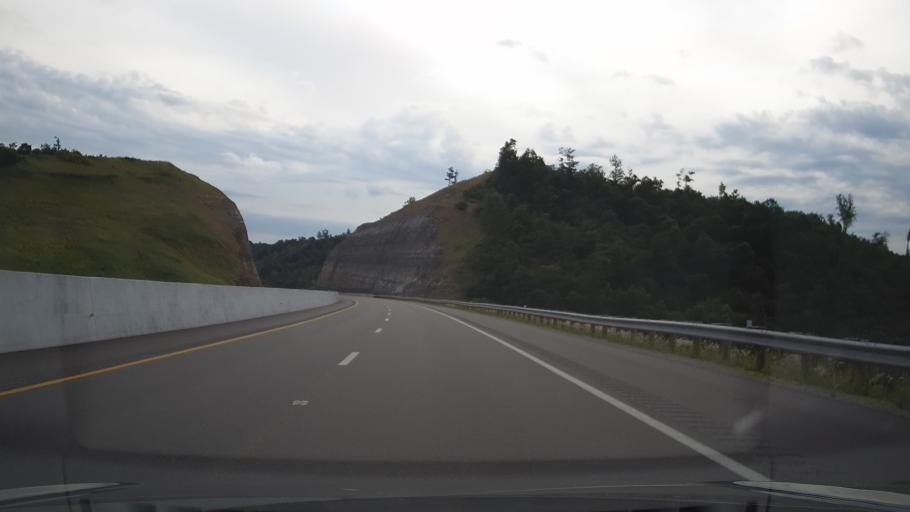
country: US
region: Ohio
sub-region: Scioto County
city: Lucasville
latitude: 38.8979
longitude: -82.9645
